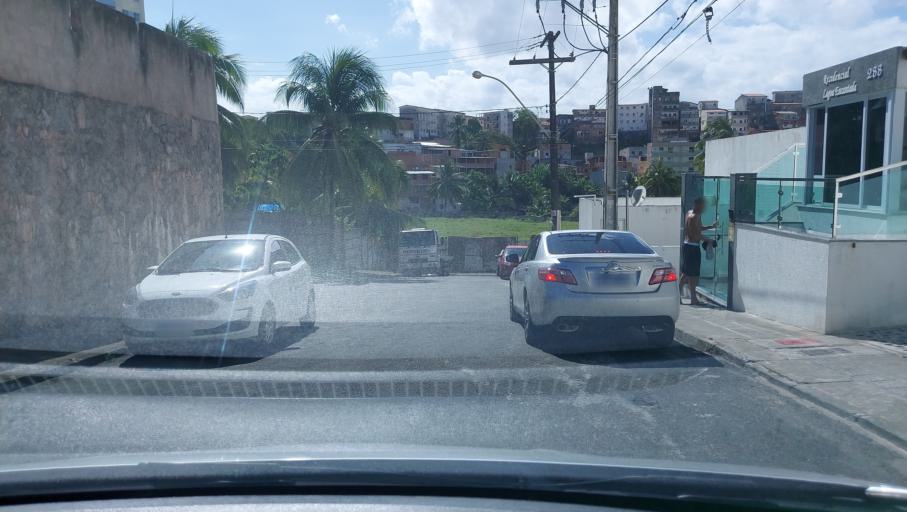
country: BR
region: Bahia
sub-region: Salvador
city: Salvador
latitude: -12.9632
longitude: -38.4380
